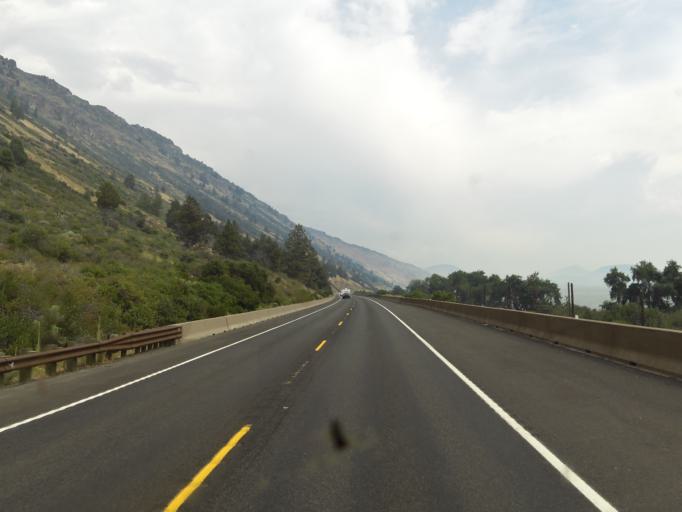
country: US
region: Oregon
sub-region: Klamath County
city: Klamath Falls
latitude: 42.4189
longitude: -121.8438
